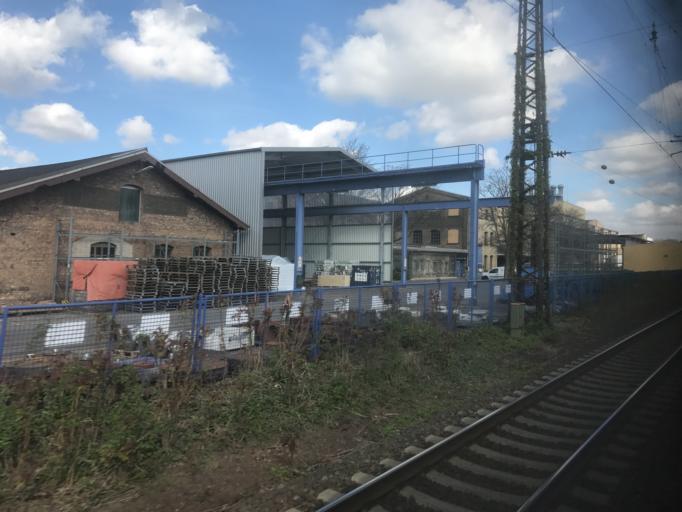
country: DE
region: Rheinland-Pfalz
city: Frankenthal
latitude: 49.5407
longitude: 8.3497
